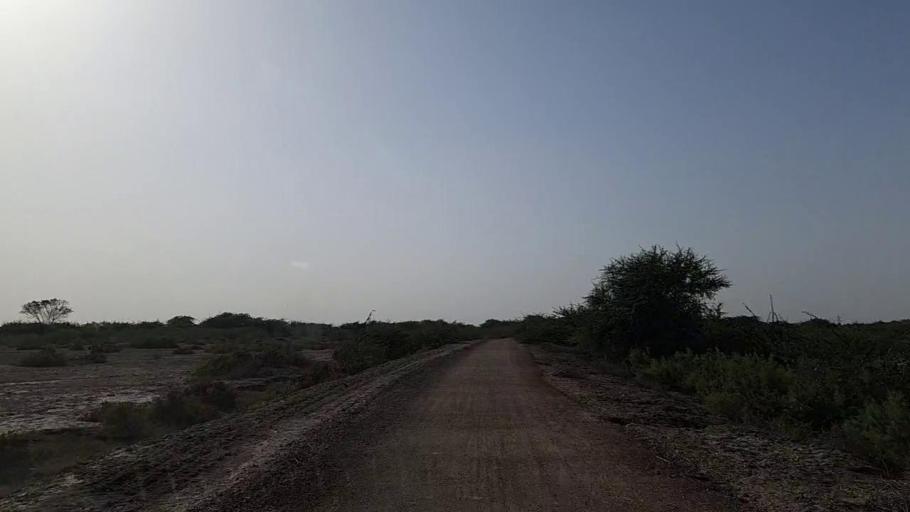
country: PK
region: Sindh
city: Jati
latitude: 24.2875
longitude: 68.2107
